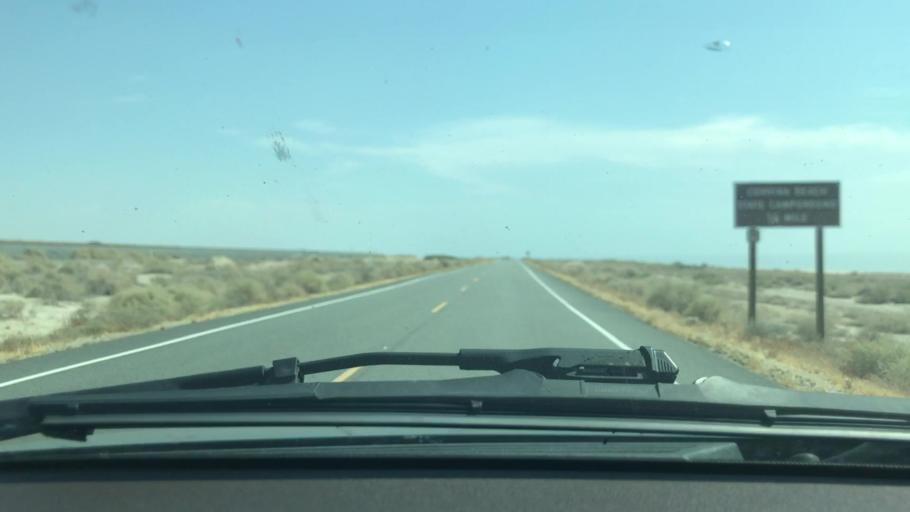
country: US
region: California
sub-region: Imperial County
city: Desert Shores
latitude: 33.4798
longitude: -115.8911
